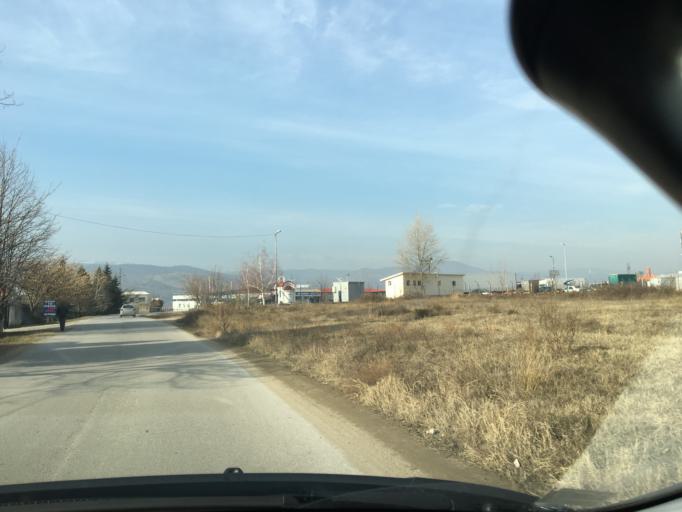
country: BG
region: Blagoevgrad
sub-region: Obshtina Sandanski
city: Sandanski
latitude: 41.5066
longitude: 23.2787
